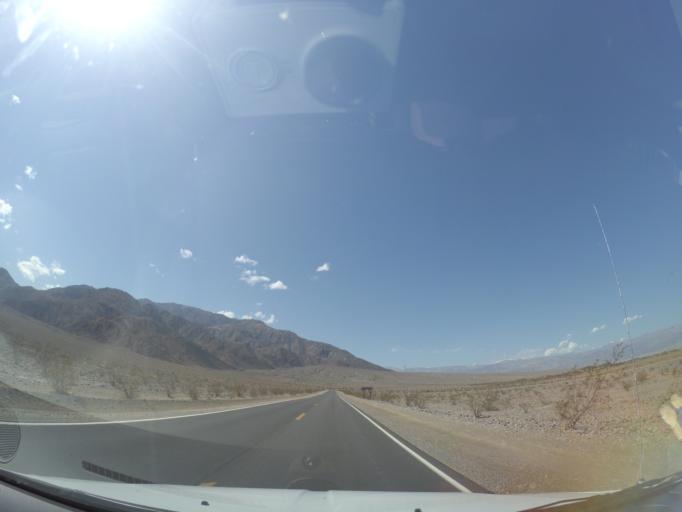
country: US
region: Nevada
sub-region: Nye County
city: Beatty
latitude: 36.6090
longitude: -117.0904
